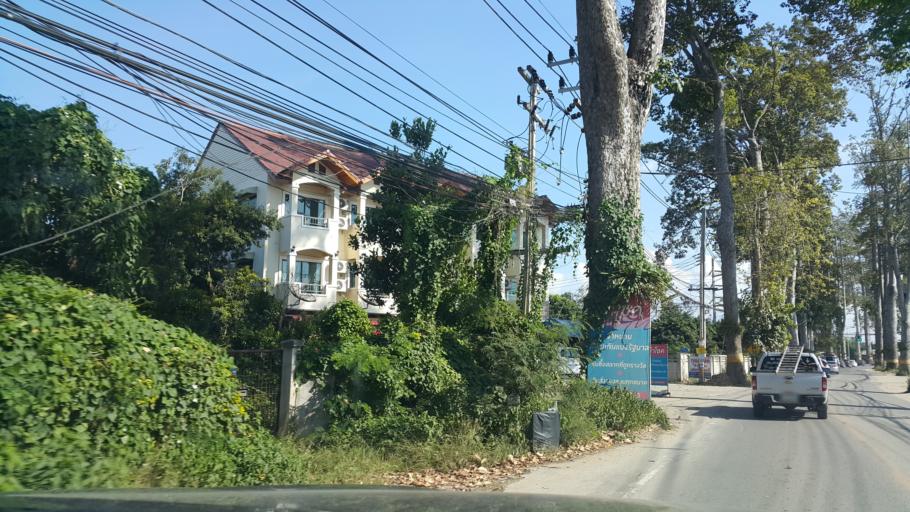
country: TH
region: Chiang Mai
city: Saraphi
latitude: 18.7307
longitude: 99.0220
